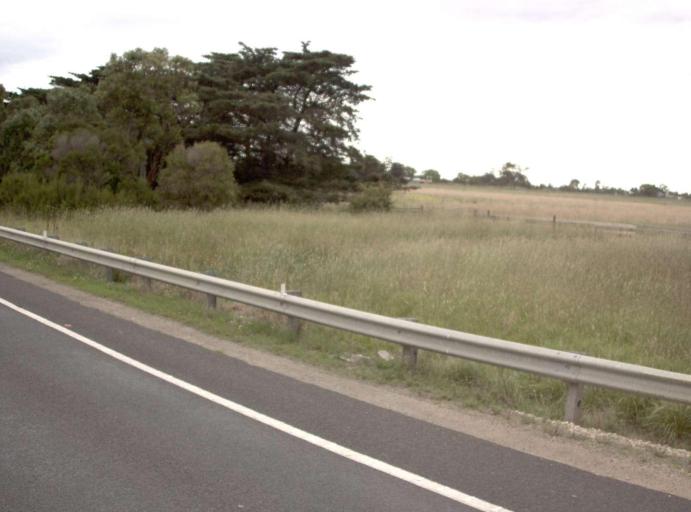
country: AU
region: Victoria
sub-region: Wellington
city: Sale
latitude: -38.0727
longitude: 147.0730
